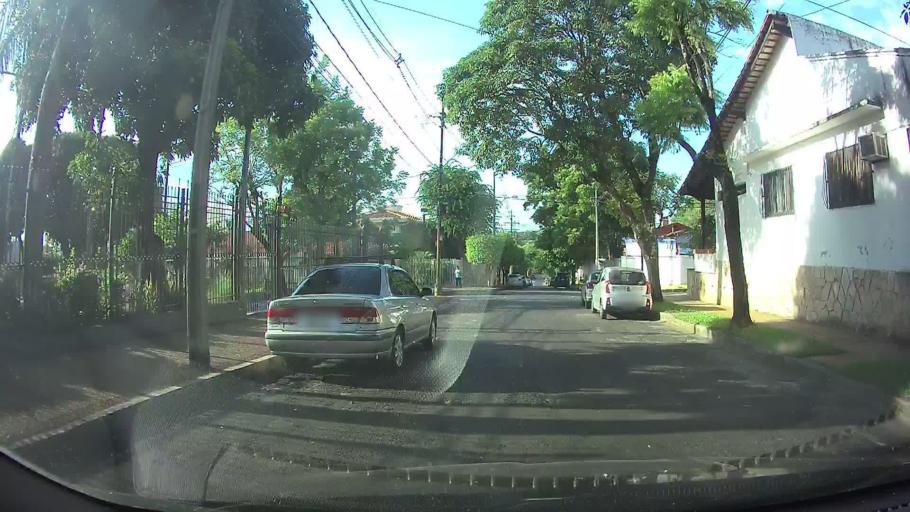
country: PY
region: Asuncion
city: Asuncion
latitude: -25.2871
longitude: -57.6035
